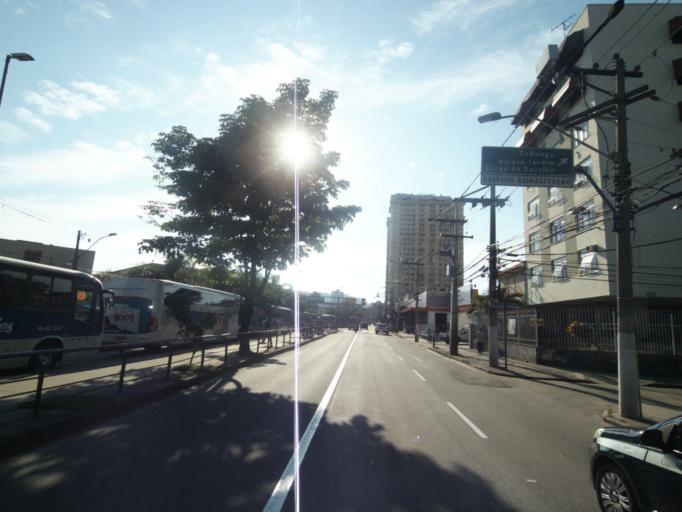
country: BR
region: Rio de Janeiro
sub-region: Niteroi
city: Niteroi
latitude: -22.8811
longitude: -43.0947
